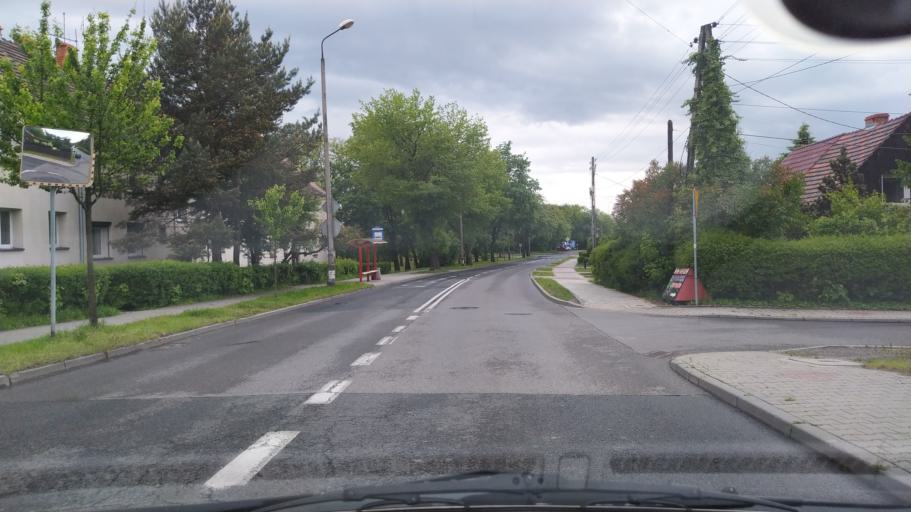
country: PL
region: Silesian Voivodeship
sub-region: Gliwice
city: Gliwice
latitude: 50.2911
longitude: 18.7201
